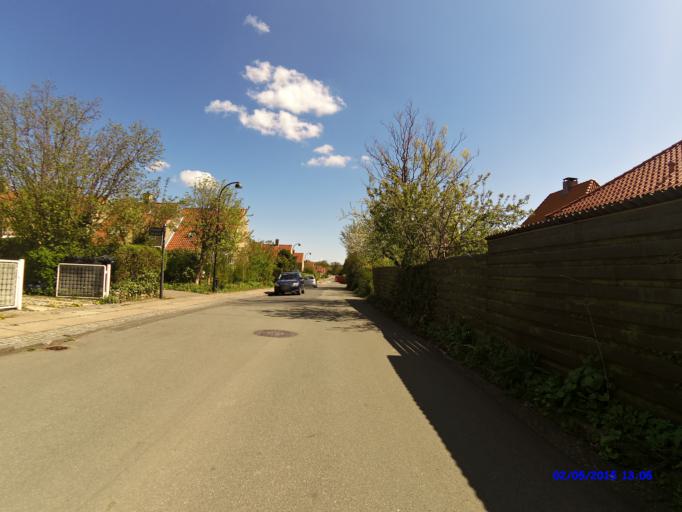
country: DK
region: Capital Region
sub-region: Lyngby-Tarbaek Kommune
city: Kongens Lyngby
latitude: 55.7289
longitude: 12.5276
